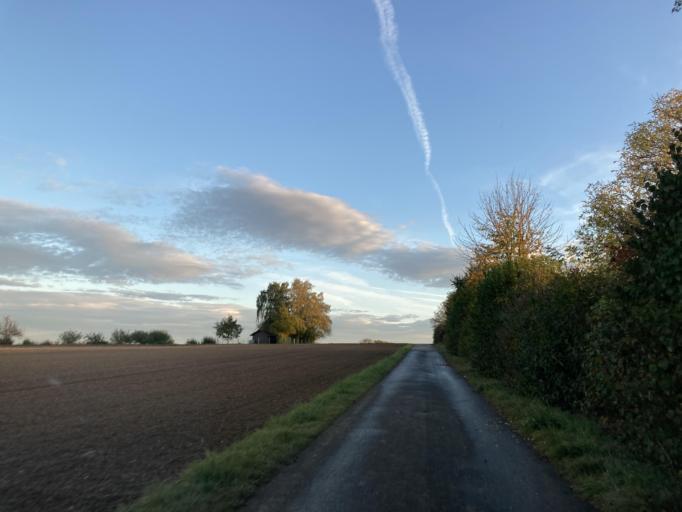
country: DE
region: Baden-Wuerttemberg
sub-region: Regierungsbezirk Stuttgart
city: Bondorf
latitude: 48.4871
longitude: 8.8012
